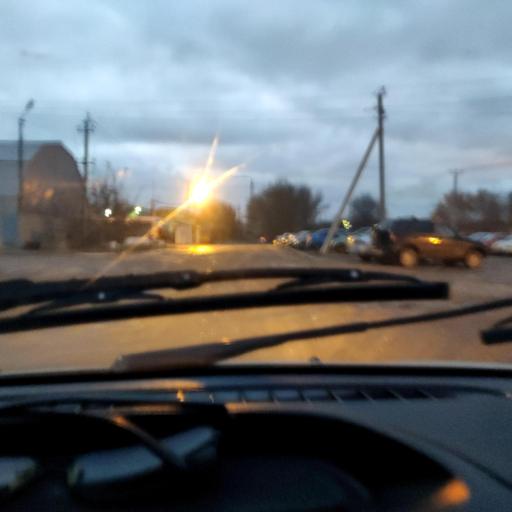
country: RU
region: Samara
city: Tol'yatti
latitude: 53.5658
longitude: 49.4835
